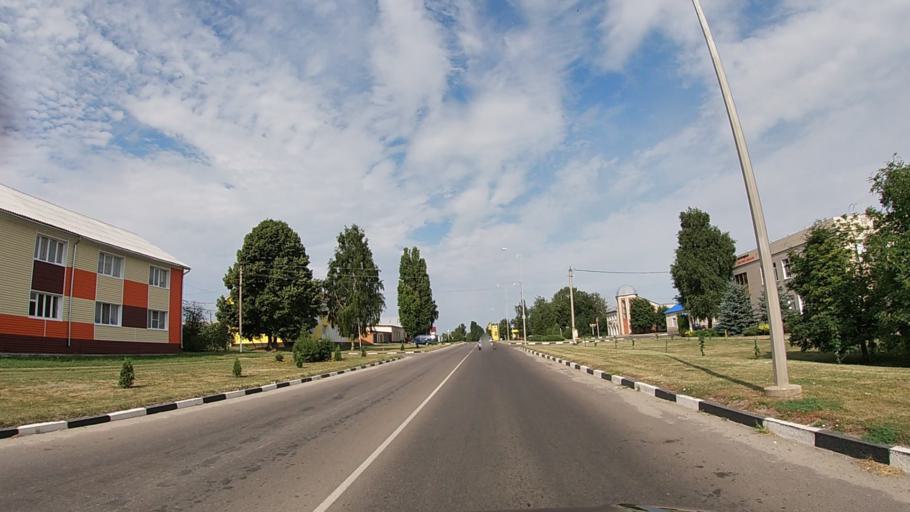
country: RU
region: Belgorod
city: Krasnaya Yaruga
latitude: 50.7983
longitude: 35.6448
